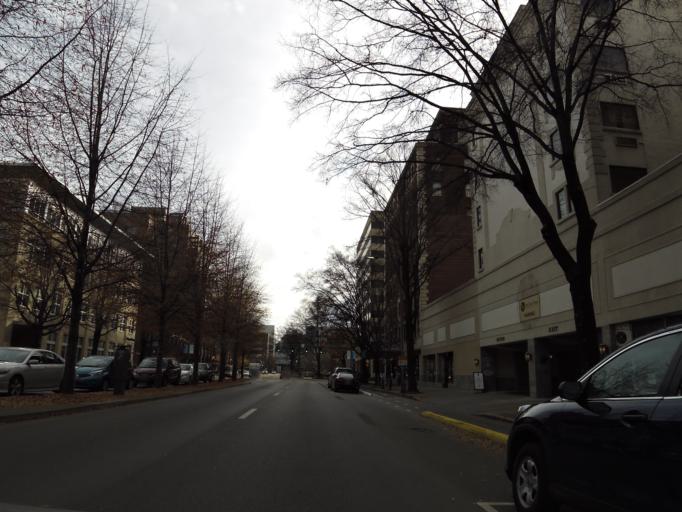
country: US
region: Tennessee
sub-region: Hamilton County
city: Chattanooga
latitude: 35.0466
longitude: -85.3106
